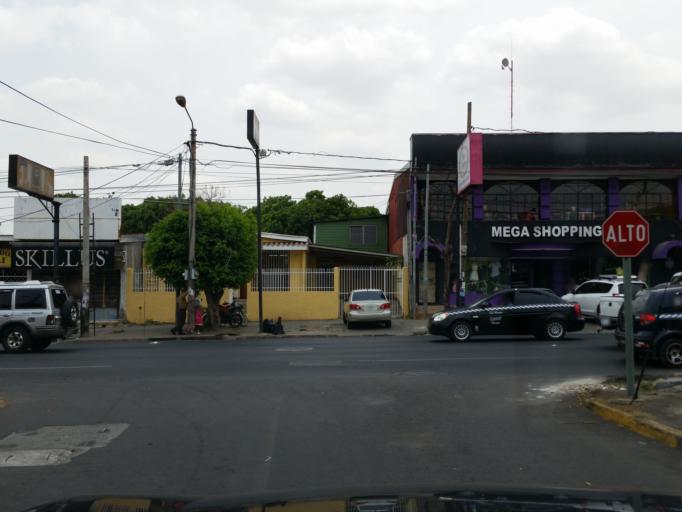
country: NI
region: Managua
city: Managua
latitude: 12.1455
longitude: -86.2305
